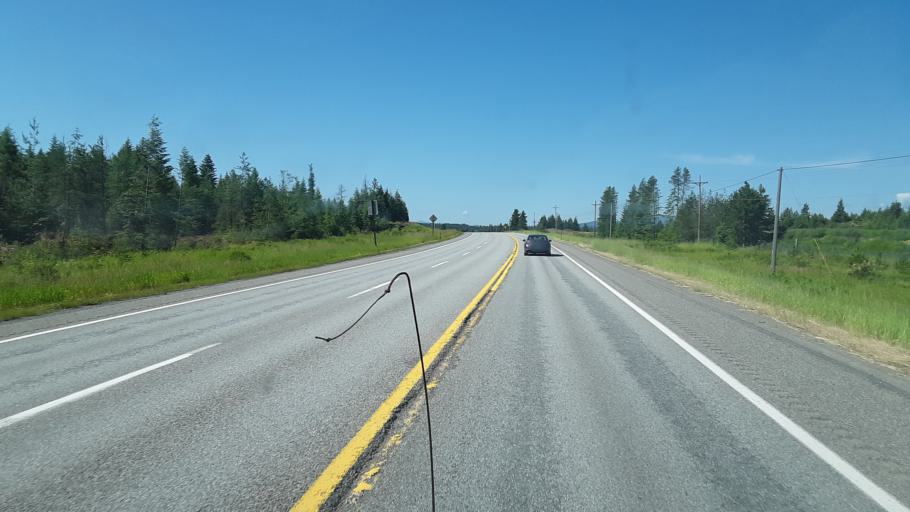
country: US
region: Idaho
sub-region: Kootenai County
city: Spirit Lake
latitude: 48.0047
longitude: -116.6710
